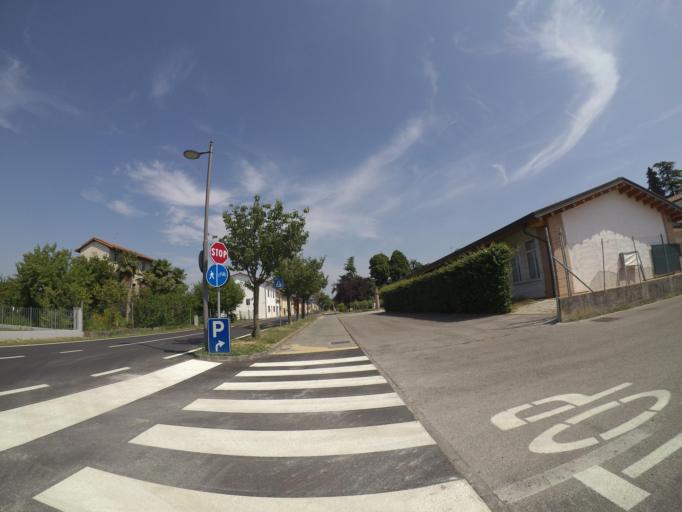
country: IT
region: Friuli Venezia Giulia
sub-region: Provincia di Pordenone
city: San Vito al Tagliamento
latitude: 45.9117
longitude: 12.8745
